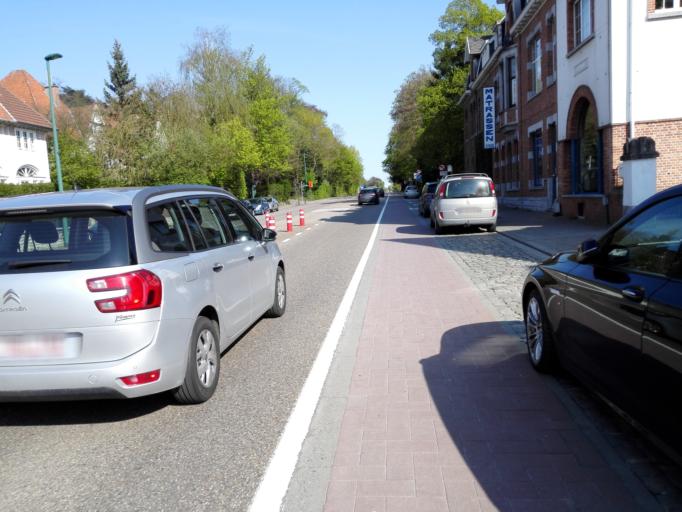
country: BE
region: Flanders
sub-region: Provincie Vlaams-Brabant
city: Leuven
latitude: 50.8705
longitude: 4.7279
